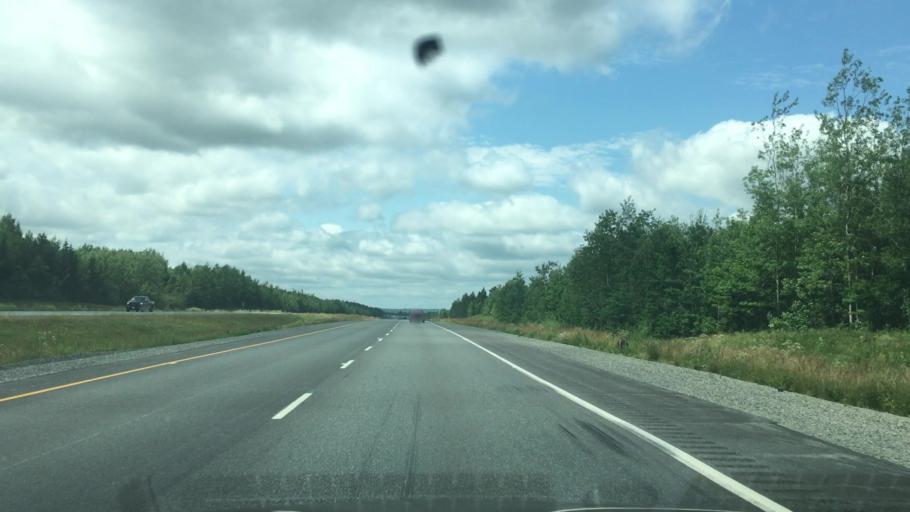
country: CA
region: Nova Scotia
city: Oxford
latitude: 45.7120
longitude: -63.9480
